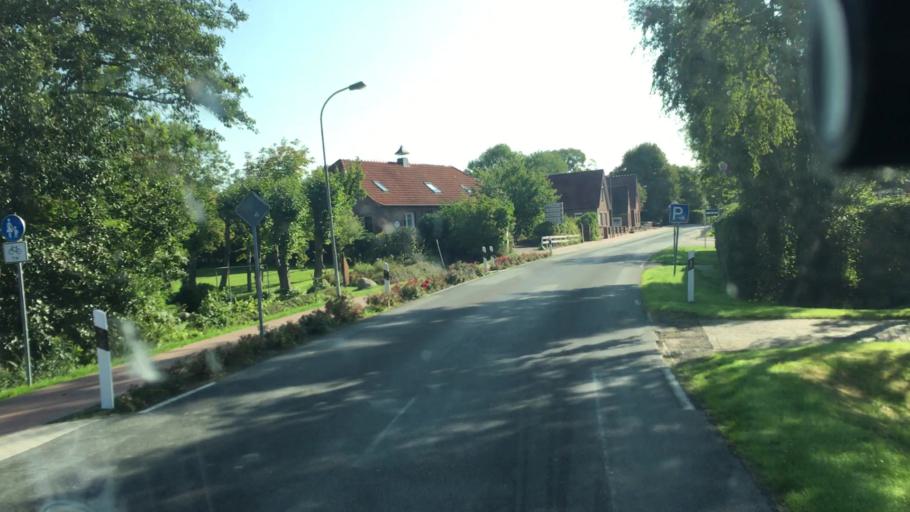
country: DE
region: Lower Saxony
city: Werdum
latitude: 53.6602
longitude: 7.7218
